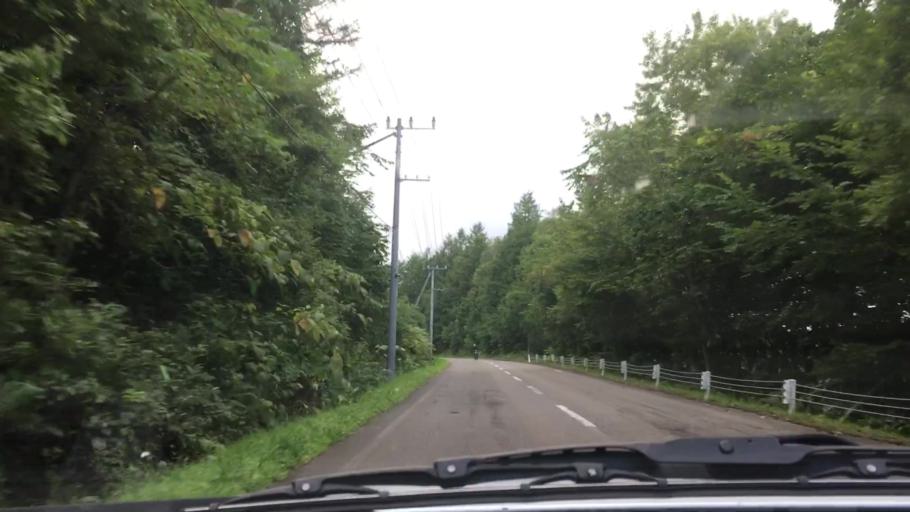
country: JP
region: Hokkaido
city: Otofuke
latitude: 43.1468
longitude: 142.8728
